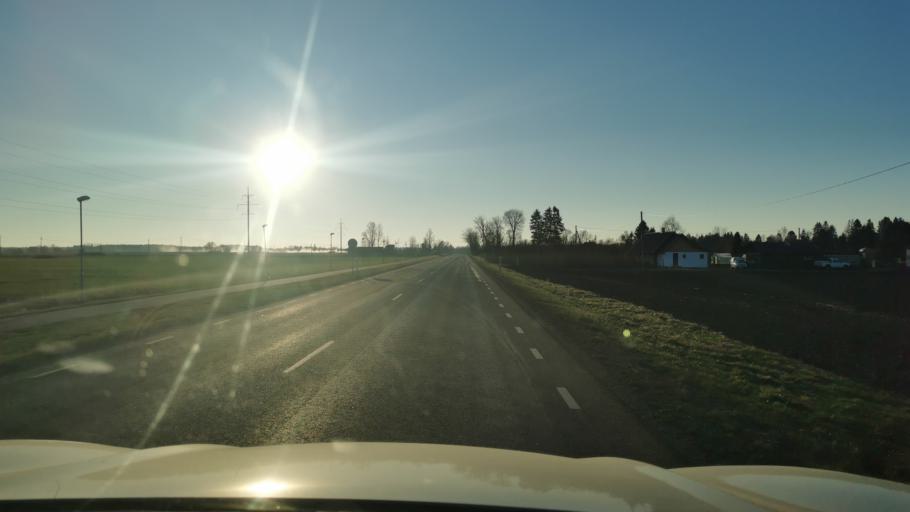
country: EE
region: Ida-Virumaa
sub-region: Kivioli linn
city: Kivioli
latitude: 59.3328
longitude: 27.0107
